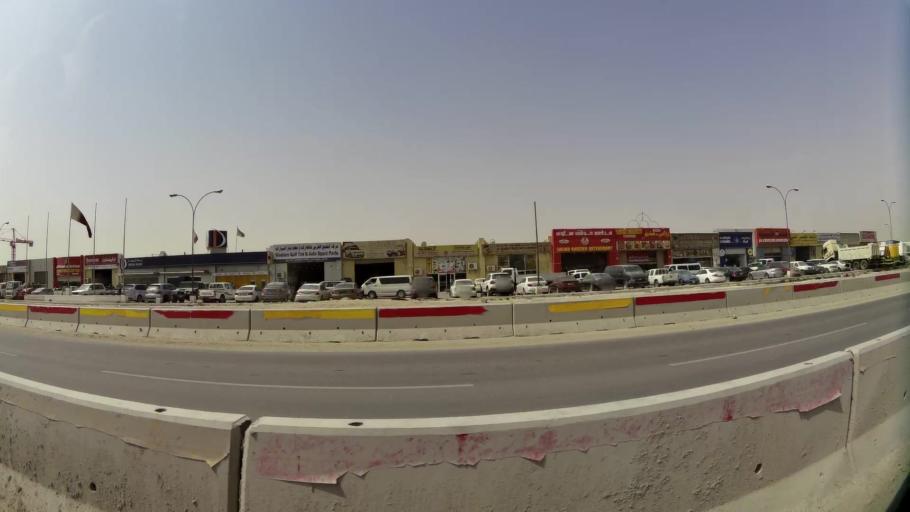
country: QA
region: Baladiyat ar Rayyan
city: Ar Rayyan
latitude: 25.1900
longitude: 51.4354
